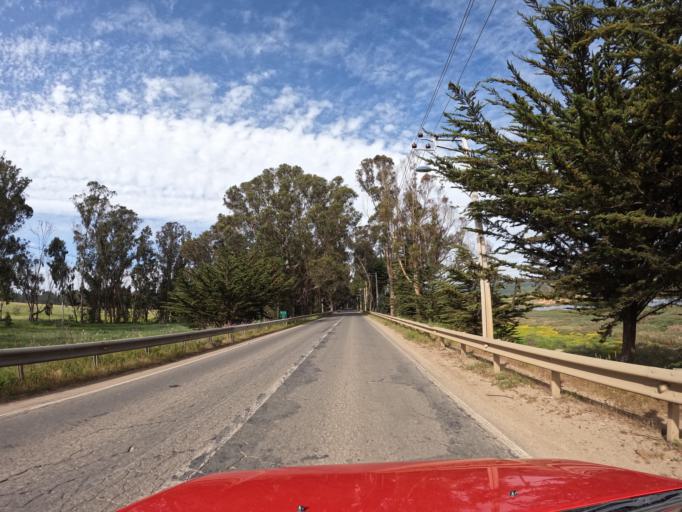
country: CL
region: O'Higgins
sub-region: Provincia de Colchagua
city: Santa Cruz
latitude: -34.3854
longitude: -71.9868
